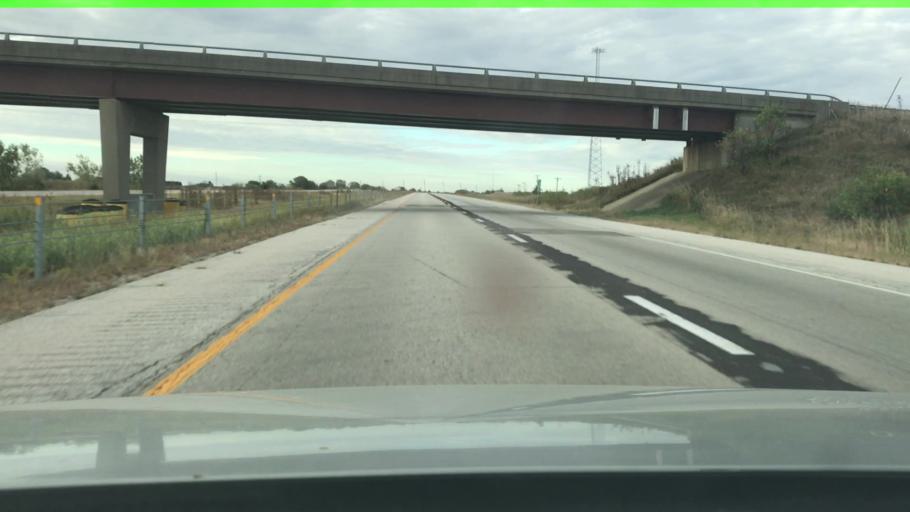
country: US
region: Illinois
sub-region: Livingston County
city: Odell
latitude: 40.9916
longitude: -88.5411
